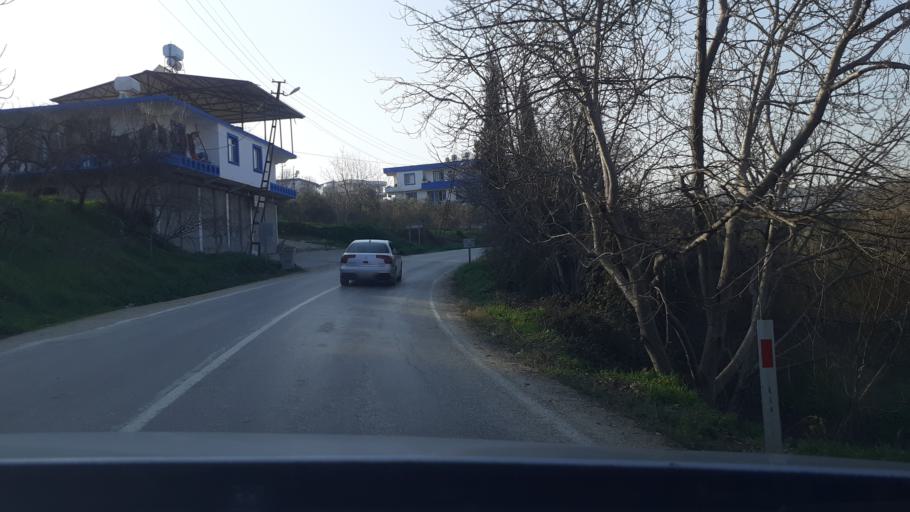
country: TR
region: Hatay
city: Fatikli
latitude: 36.1107
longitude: 36.2662
